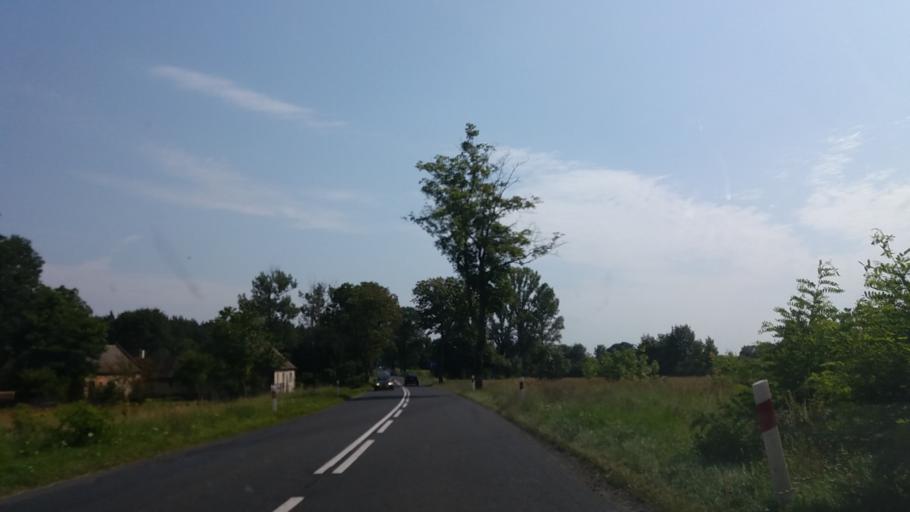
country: PL
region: Lubusz
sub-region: Powiat strzelecko-drezdenecki
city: Zwierzyn
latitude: 52.8457
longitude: 15.5538
